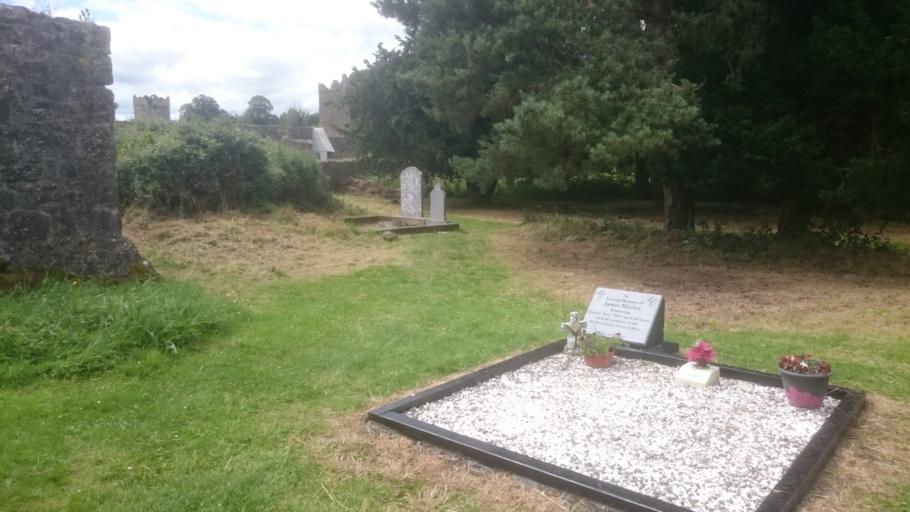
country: IE
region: Leinster
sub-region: Kilkenny
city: Kilkenny
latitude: 52.5392
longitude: -7.2669
